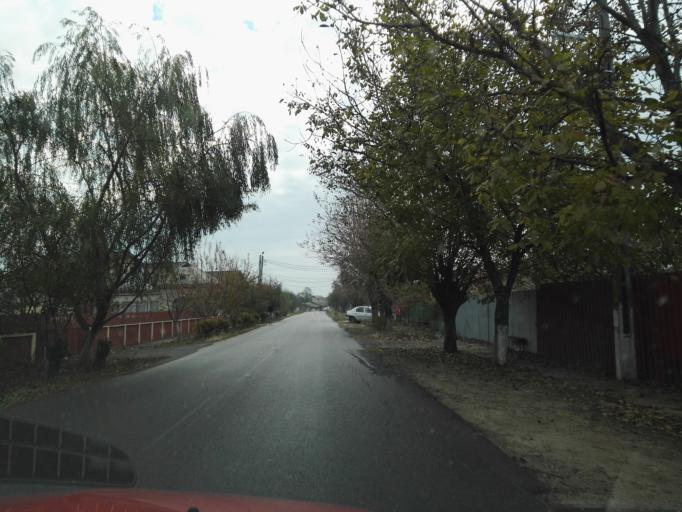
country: RO
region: Ilfov
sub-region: Comuna Magurele
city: Alunisu
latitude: 44.3376
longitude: 26.0592
